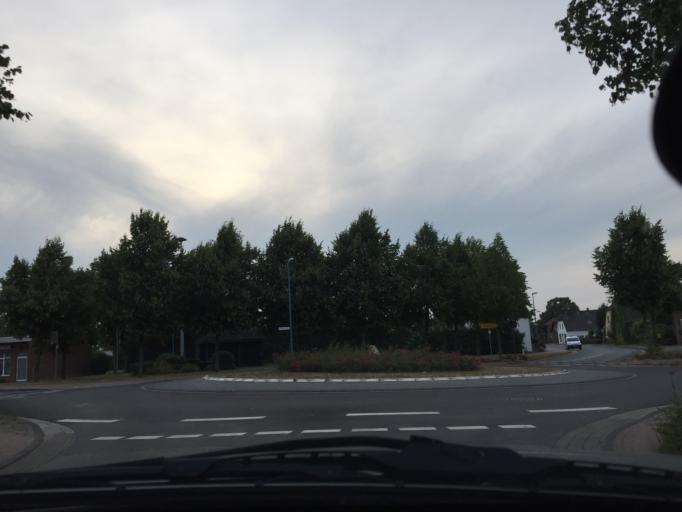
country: DE
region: North Rhine-Westphalia
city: Kalkar
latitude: 51.7631
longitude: 6.2575
